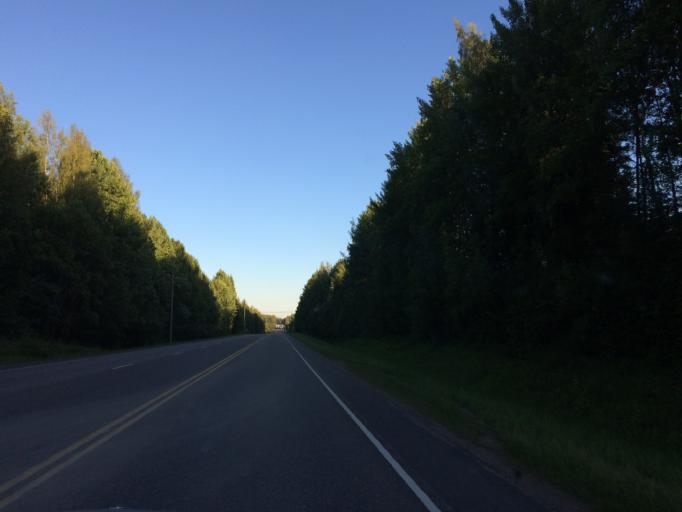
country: FI
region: Haeme
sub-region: Riihimaeki
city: Riihimaeki
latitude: 60.7604
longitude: 24.7163
